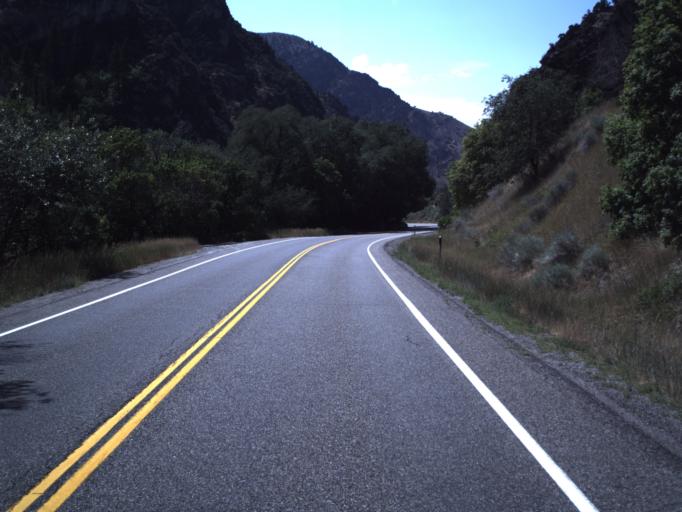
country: US
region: Utah
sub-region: Cache County
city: North Logan
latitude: 41.7451
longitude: -111.7512
